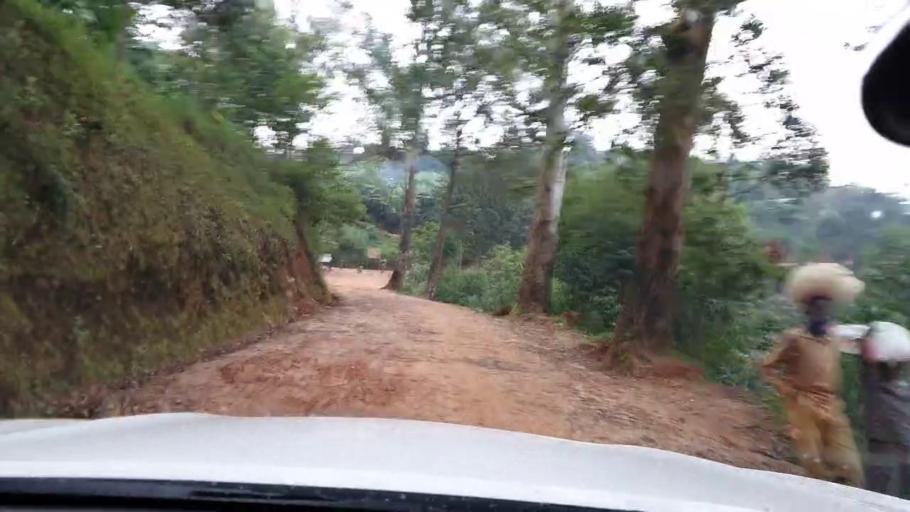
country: RW
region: Western Province
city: Cyangugu
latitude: -2.4065
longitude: 29.2090
